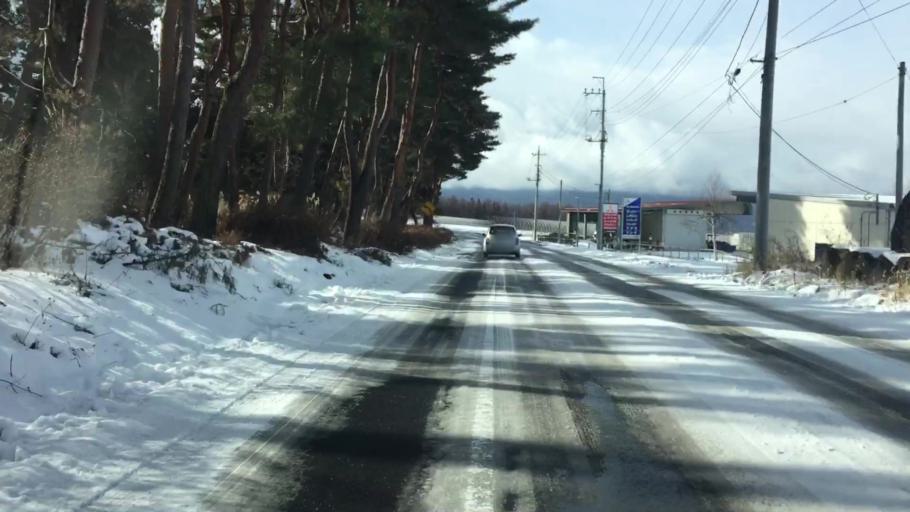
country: JP
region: Gunma
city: Numata
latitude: 36.6263
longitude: 139.0926
